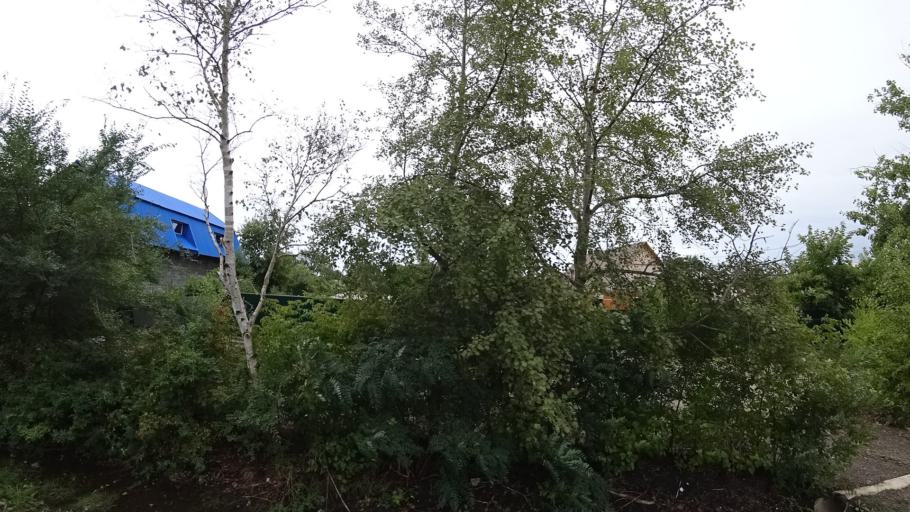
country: RU
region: Primorskiy
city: Chernigovka
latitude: 44.3333
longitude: 132.5695
